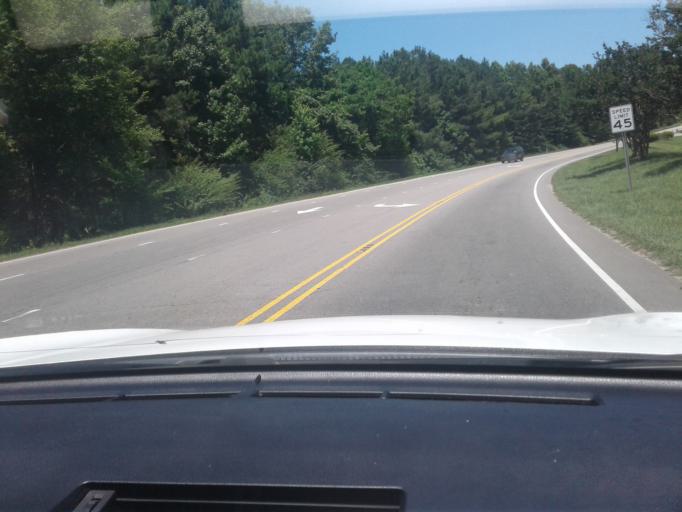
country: US
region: North Carolina
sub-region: Harnett County
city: Erwin
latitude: 35.3114
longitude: -78.6964
